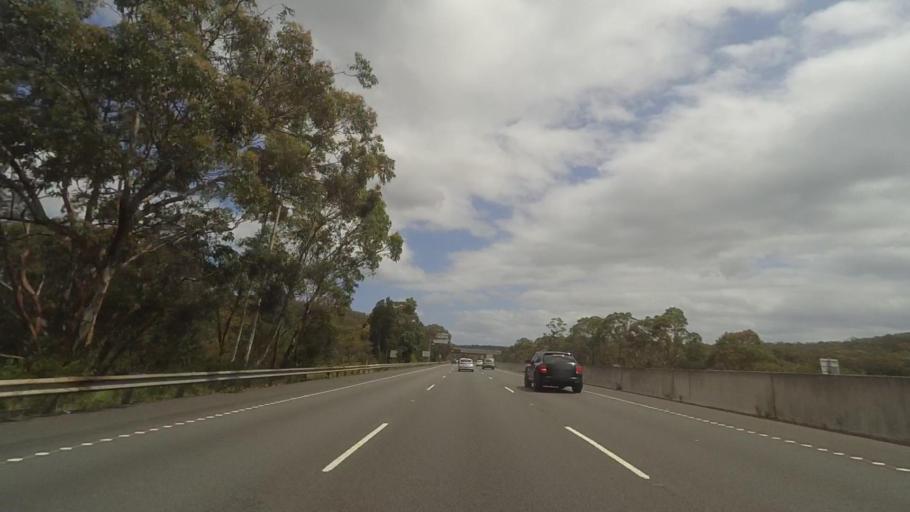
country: AU
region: New South Wales
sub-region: Gosford Shire
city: Point Clare
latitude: -33.4420
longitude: 151.2185
